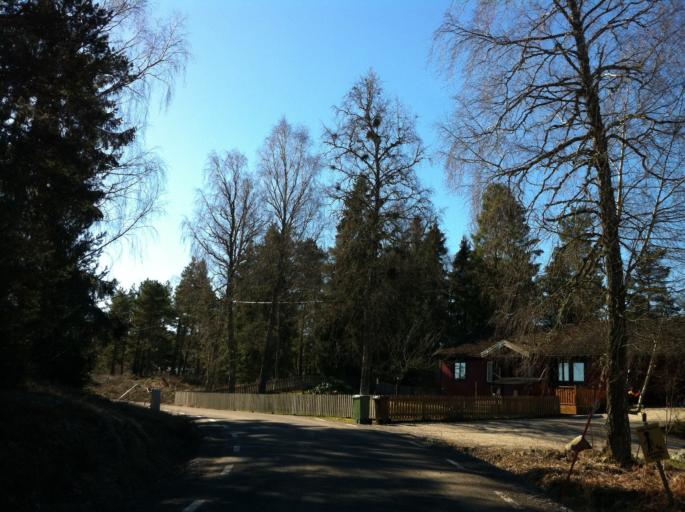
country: SE
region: Vaestra Goetaland
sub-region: Grastorps Kommun
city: Graestorp
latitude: 58.4573
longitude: 12.6213
